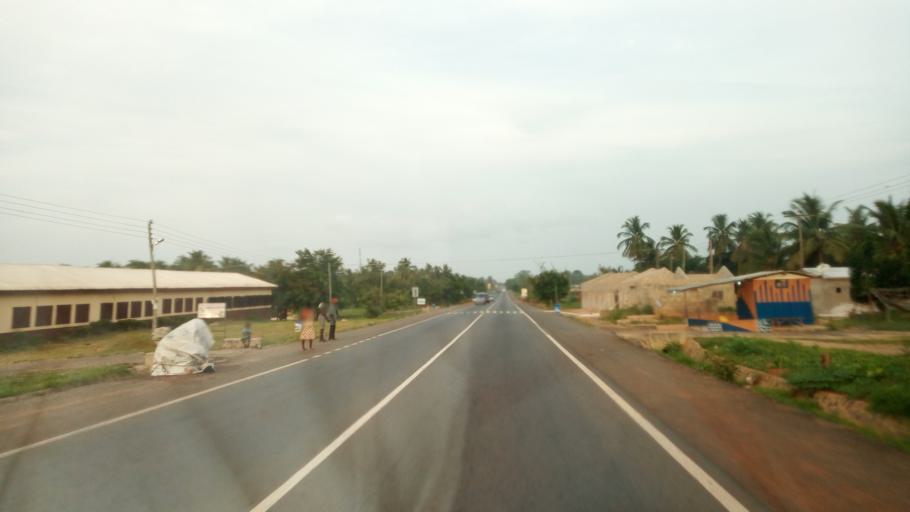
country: TG
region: Maritime
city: Lome
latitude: 6.0956
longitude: 1.0829
